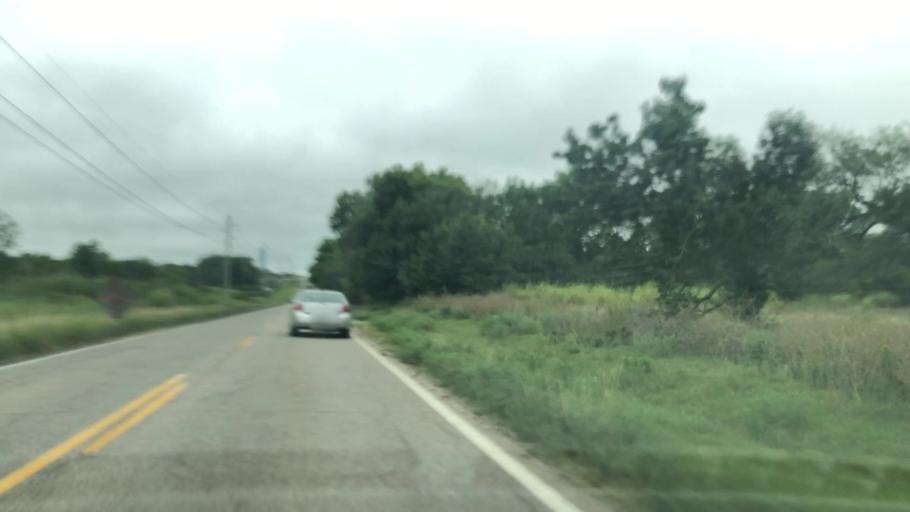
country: US
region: Oklahoma
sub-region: Washington County
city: Dewey
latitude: 36.7280
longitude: -95.8470
